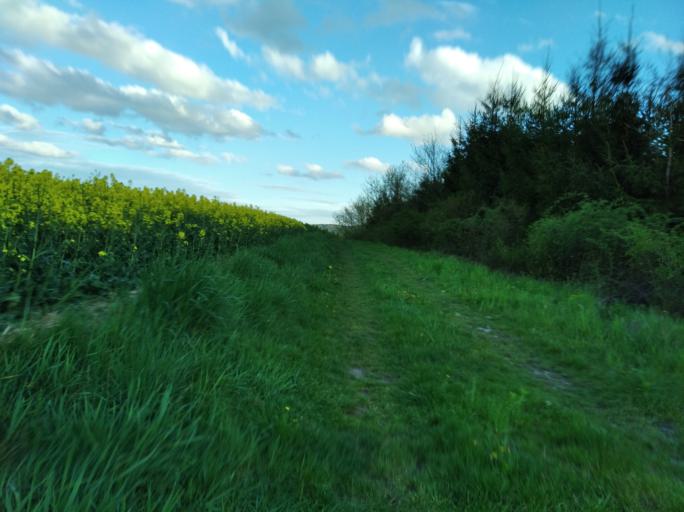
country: PL
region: Subcarpathian Voivodeship
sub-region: Powiat strzyzowski
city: Wysoka Strzyzowska
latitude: 49.8588
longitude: 21.7585
